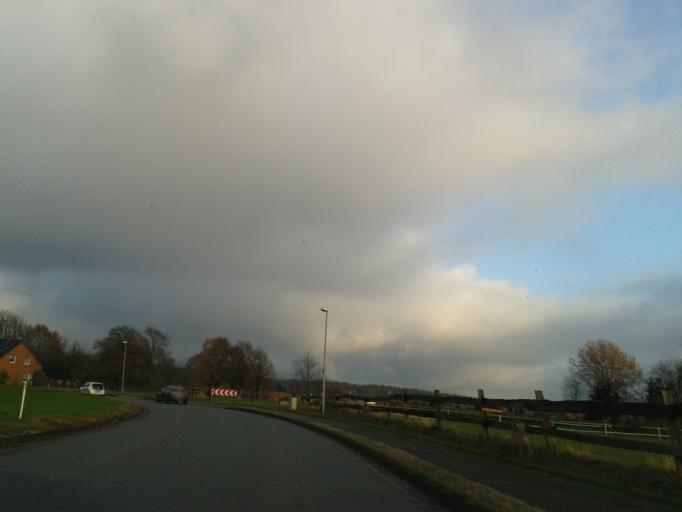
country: DE
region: North Rhine-Westphalia
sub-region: Regierungsbezirk Detmold
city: Augustdorf
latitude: 51.9040
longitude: 8.6807
